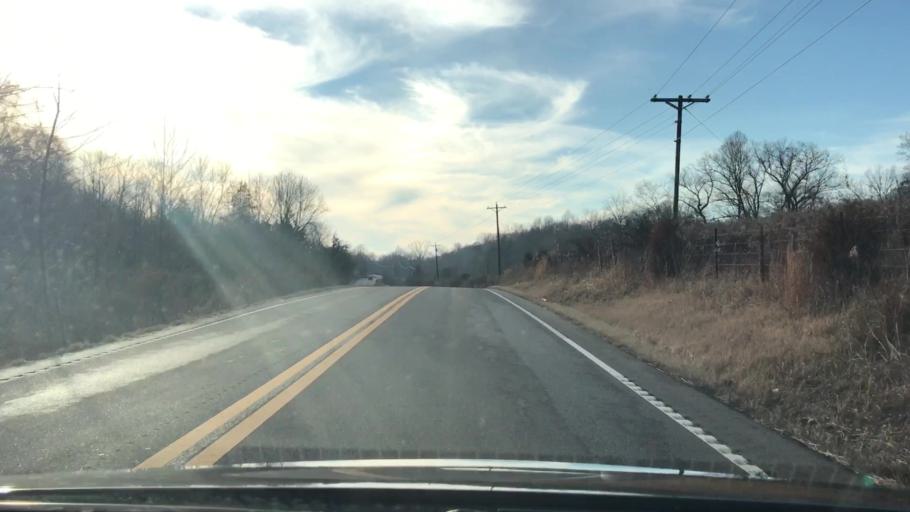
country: US
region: Tennessee
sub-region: Macon County
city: Red Boiling Springs
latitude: 36.6174
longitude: -85.7955
